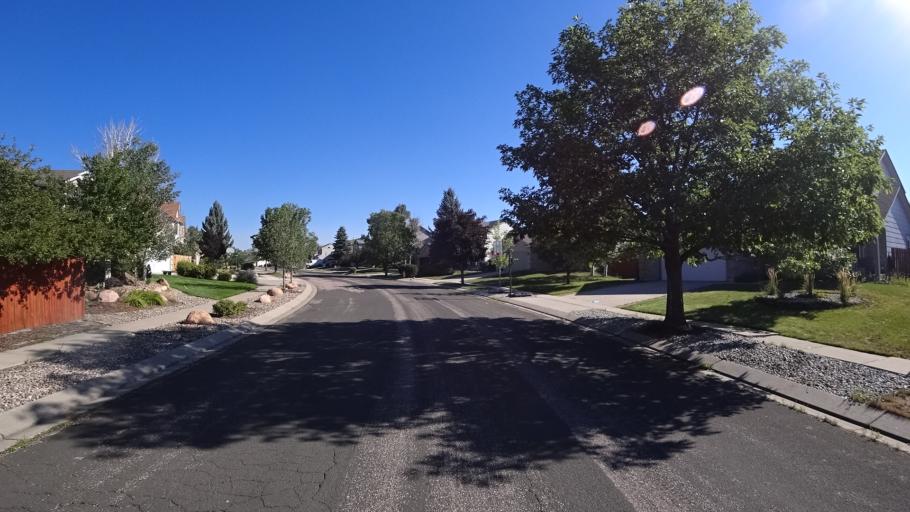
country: US
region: Colorado
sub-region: El Paso County
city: Black Forest
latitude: 38.9599
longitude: -104.7536
